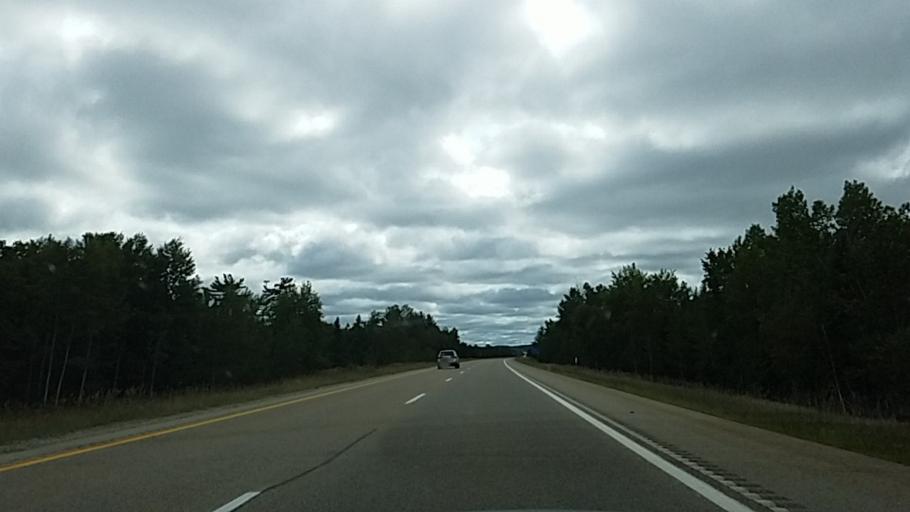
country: US
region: Michigan
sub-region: Roscommon County
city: Roscommon
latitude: 44.5234
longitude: -84.6713
